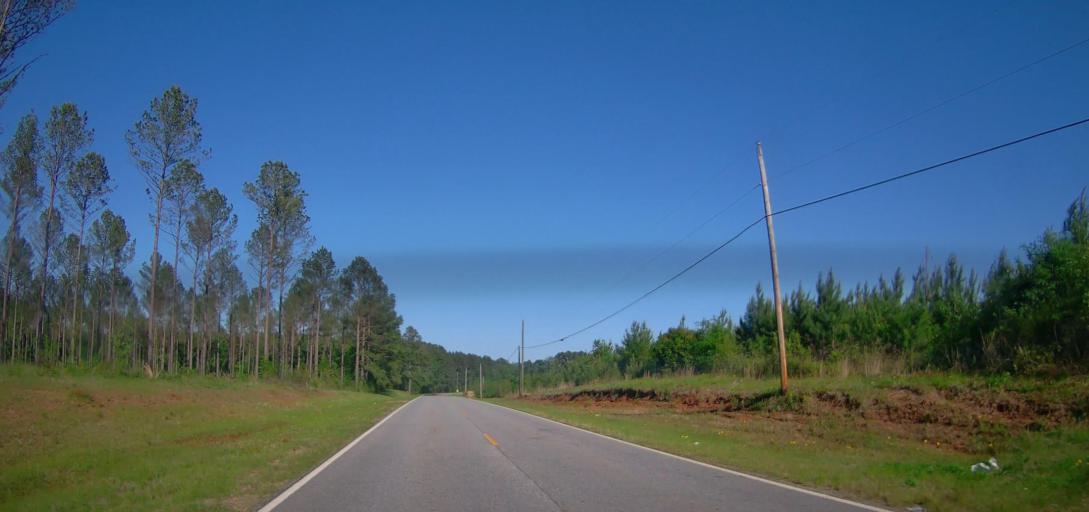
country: US
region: Georgia
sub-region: Houston County
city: Perry
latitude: 32.4504
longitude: -83.6318
